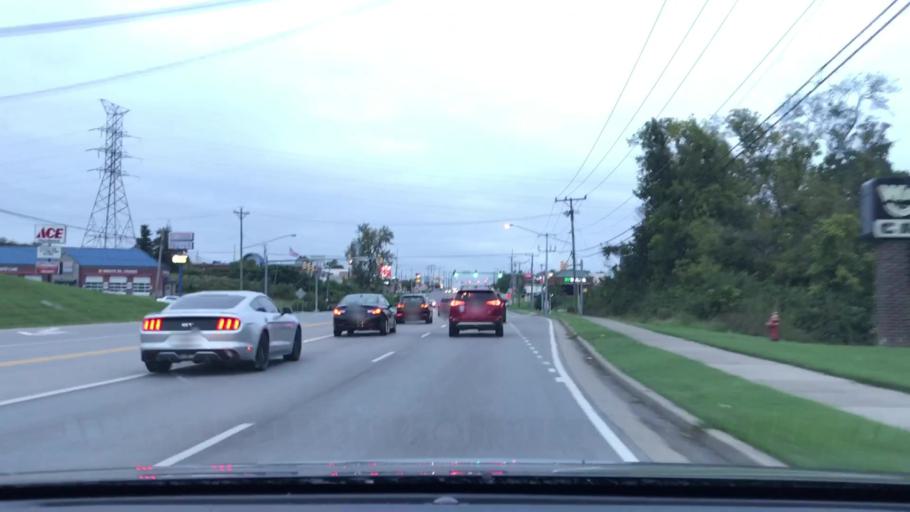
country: US
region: Tennessee
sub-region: Williamson County
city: Brentwood Estates
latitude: 36.0415
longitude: -86.7127
